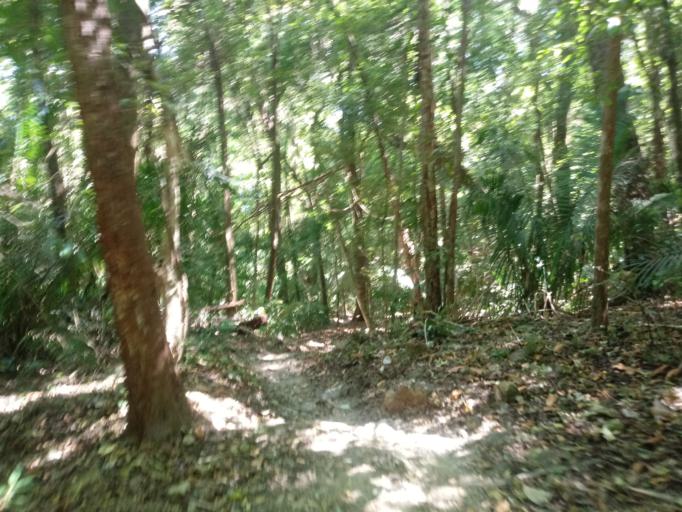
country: CR
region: Puntarenas
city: Paquera
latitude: 9.5859
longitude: -85.0959
